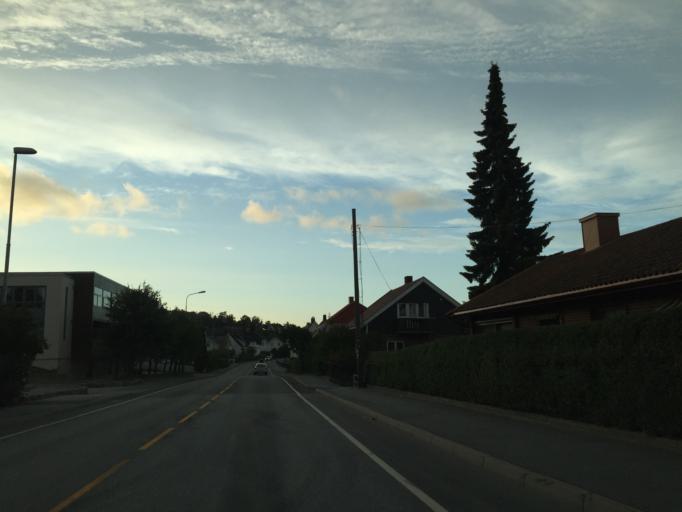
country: NO
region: Ostfold
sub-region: Fredrikstad
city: Fredrikstad
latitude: 59.2006
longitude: 10.9400
